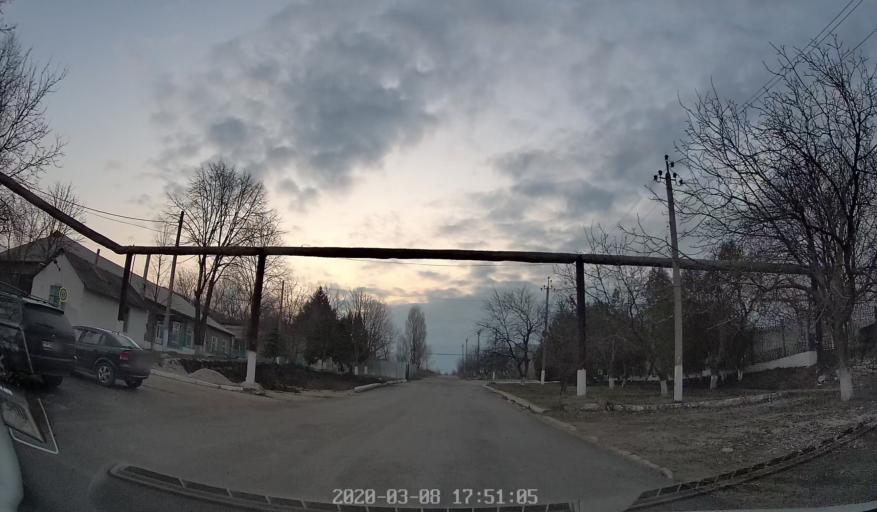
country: MD
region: Rezina
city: Rezina
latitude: 47.7539
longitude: 28.9544
